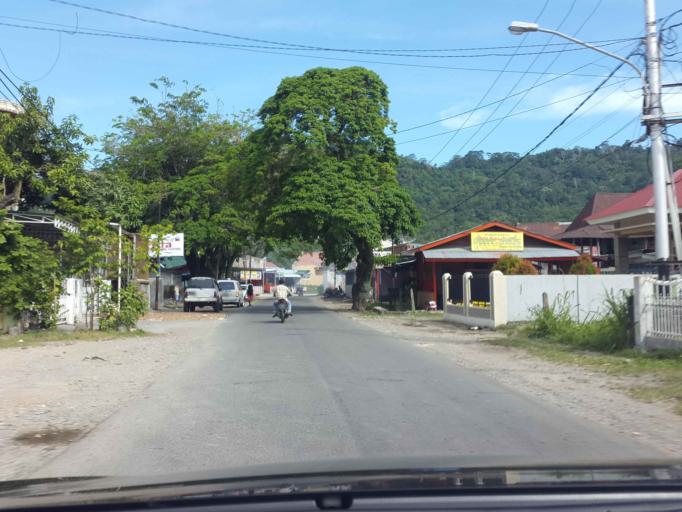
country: ID
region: West Sumatra
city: Padang
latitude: -0.9578
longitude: 100.3689
